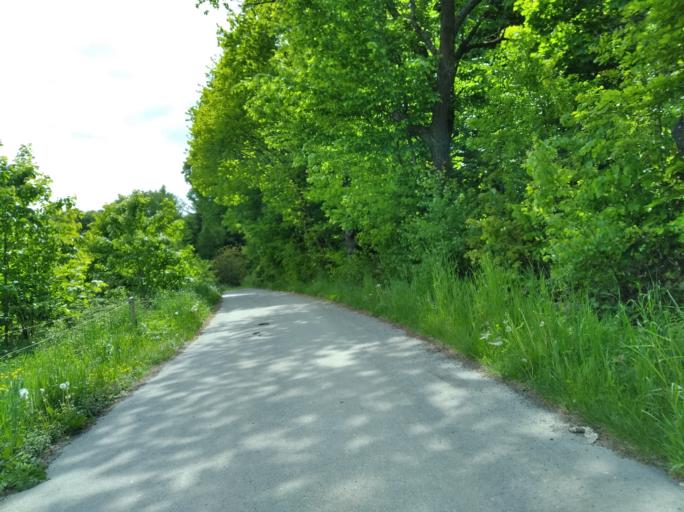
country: PL
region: Subcarpathian Voivodeship
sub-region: Powiat ropczycko-sedziszowski
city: Wielopole Skrzynskie
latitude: 49.9216
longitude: 21.6186
